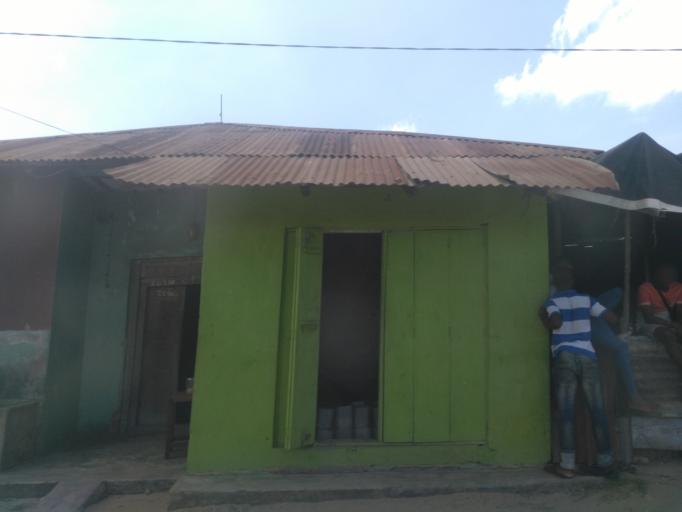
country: TZ
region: Zanzibar Urban/West
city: Zanzibar
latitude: -6.1743
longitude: 39.2085
